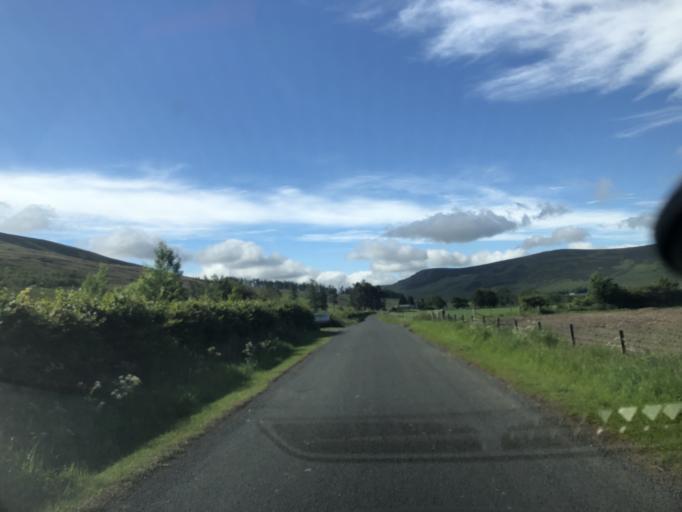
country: GB
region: Scotland
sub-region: Angus
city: Kirriemuir
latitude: 56.8138
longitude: -3.0333
